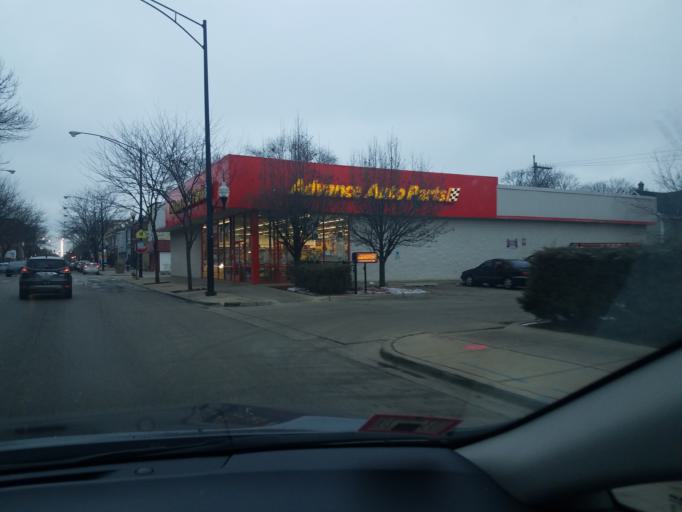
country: US
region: Illinois
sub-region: Cook County
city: Lincolnwood
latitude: 41.9612
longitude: -87.7149
